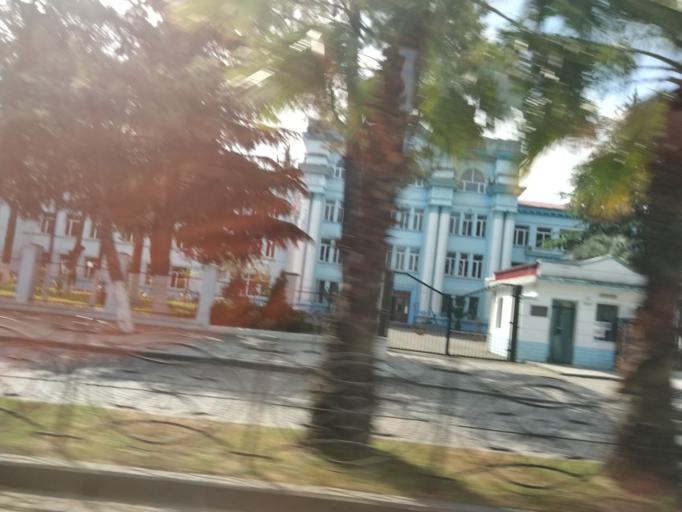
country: GE
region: Ajaria
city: Batumi
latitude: 41.6475
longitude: 41.6215
